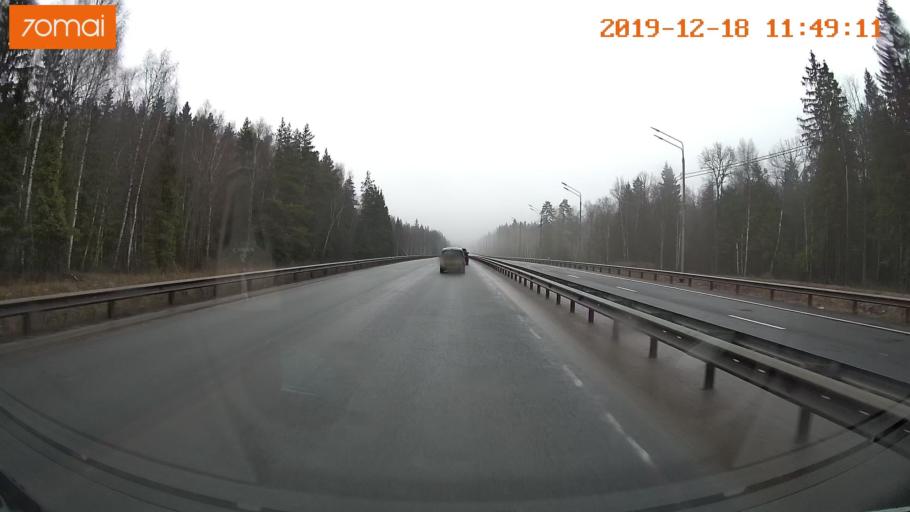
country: RU
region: Moskovskaya
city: Yershovo
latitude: 55.7754
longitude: 36.9097
